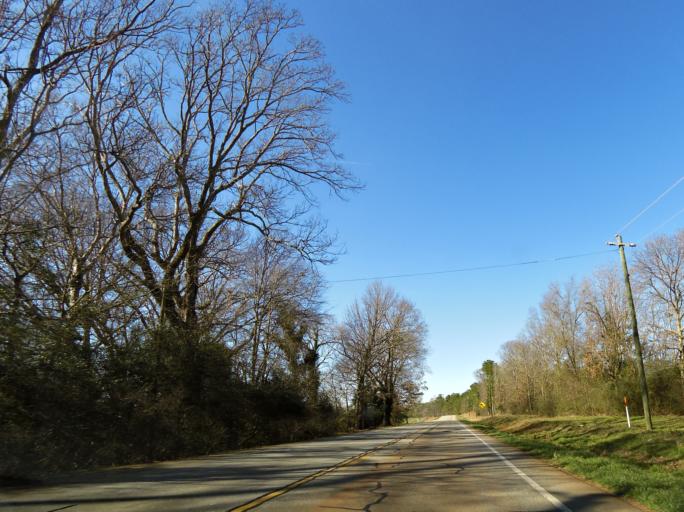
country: US
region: Georgia
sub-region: Lamar County
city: Barnesville
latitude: 32.9009
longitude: -84.1126
